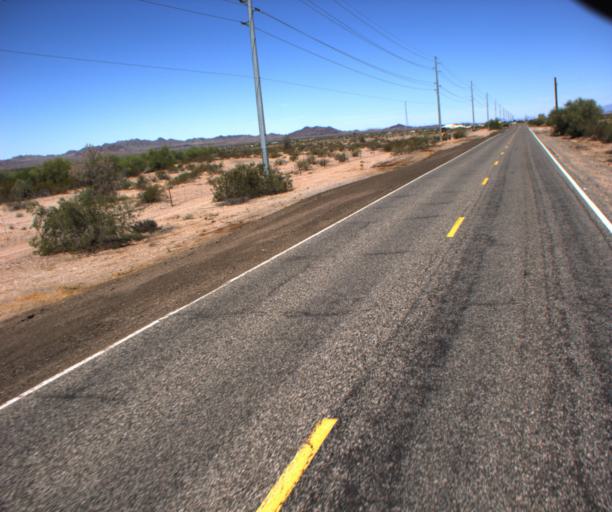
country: US
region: Arizona
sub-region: La Paz County
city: Quartzsite
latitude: 33.9034
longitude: -113.9771
